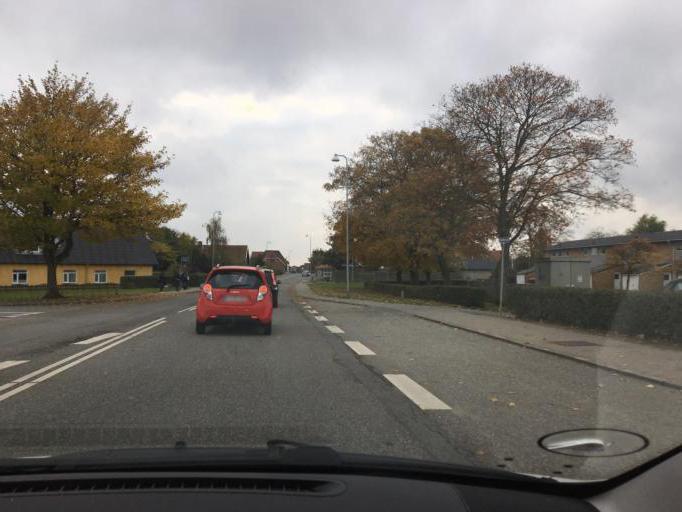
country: DK
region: South Denmark
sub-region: Fredericia Kommune
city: Fredericia
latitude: 55.5779
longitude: 9.7537
